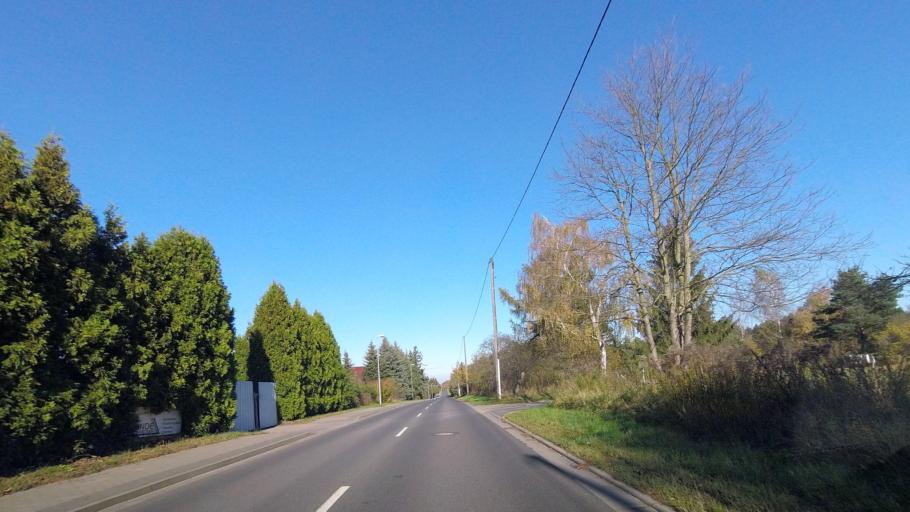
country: DE
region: Saxony-Anhalt
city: Zahna
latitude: 51.9088
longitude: 12.7743
